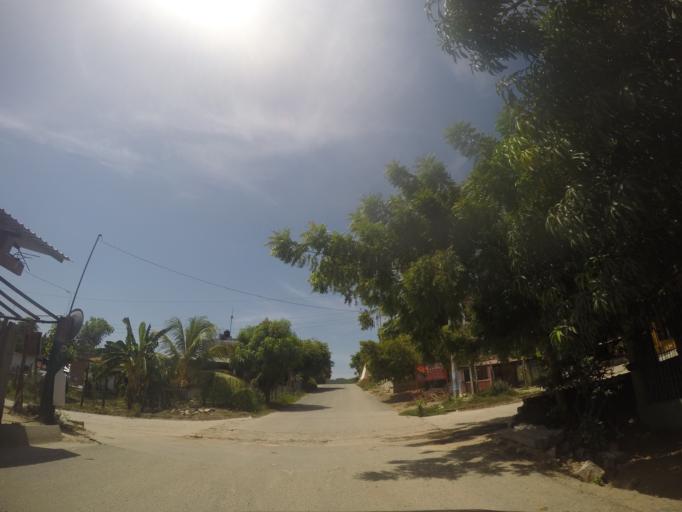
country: MX
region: Oaxaca
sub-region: Villa de Tututepec de Melchor Ocampo
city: Santa Rosa de Lima
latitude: 15.9858
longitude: -97.5500
